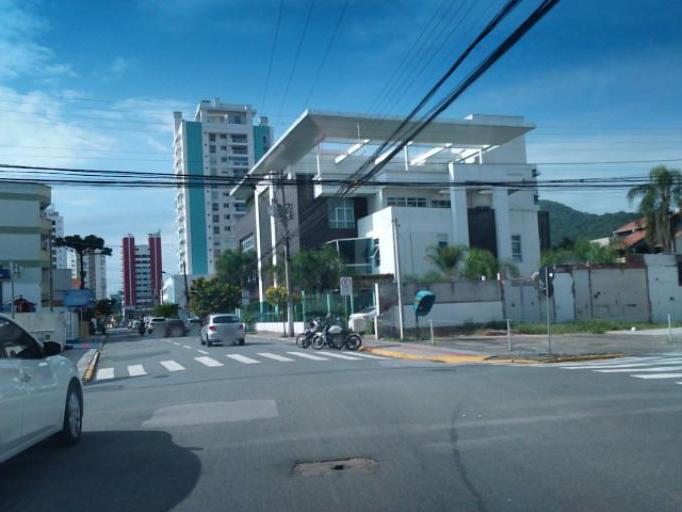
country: BR
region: Santa Catarina
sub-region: Itajai
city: Itajai
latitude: -26.9128
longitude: -48.6562
